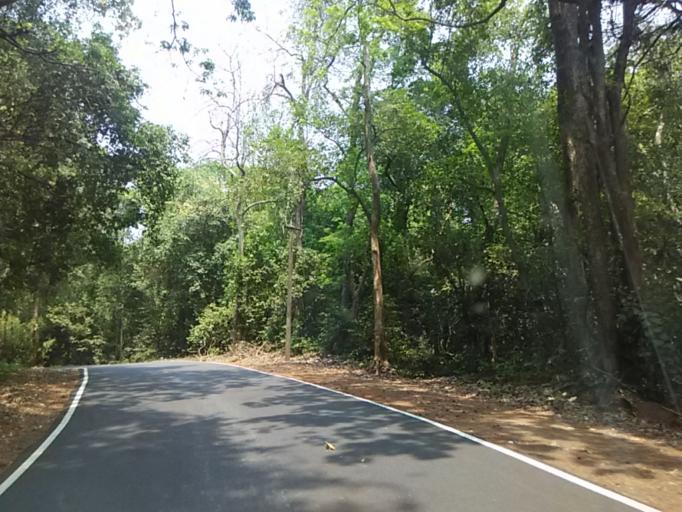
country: IN
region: Karnataka
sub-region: Kodagu
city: Virarajendrapet
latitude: 12.0771
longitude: 75.7319
